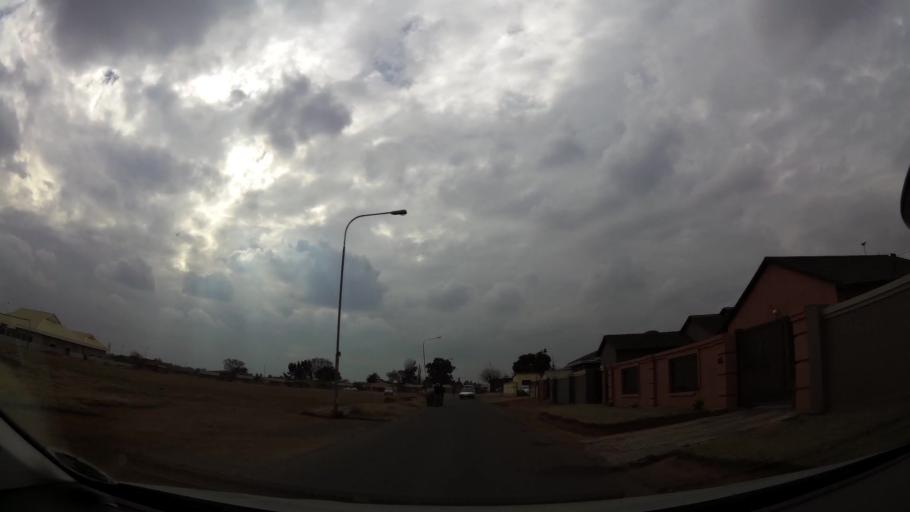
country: ZA
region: Gauteng
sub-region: City of Johannesburg Metropolitan Municipality
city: Soweto
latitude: -26.2655
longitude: 27.8503
